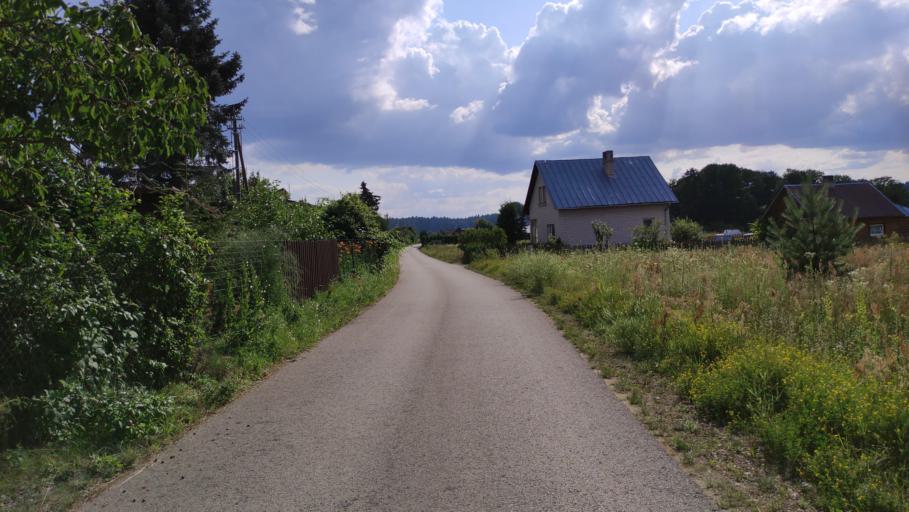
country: LT
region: Alytaus apskritis
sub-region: Alytus
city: Alytus
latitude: 54.4331
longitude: 24.0705
